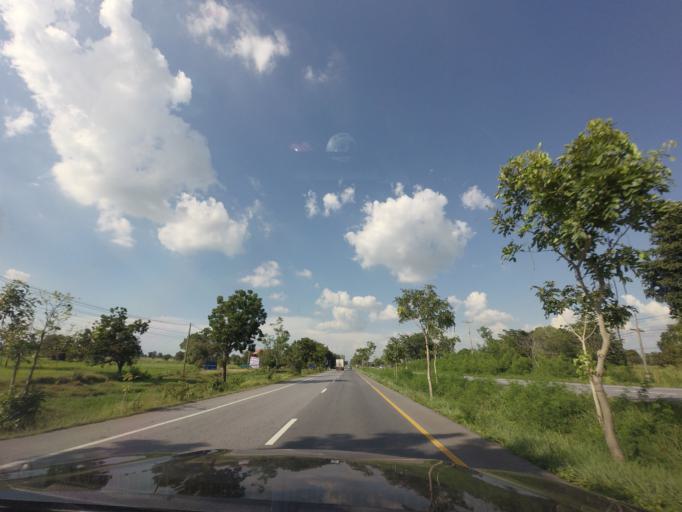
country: TH
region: Nakhon Ratchasima
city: Bua Lai
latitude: 15.7133
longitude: 102.5888
